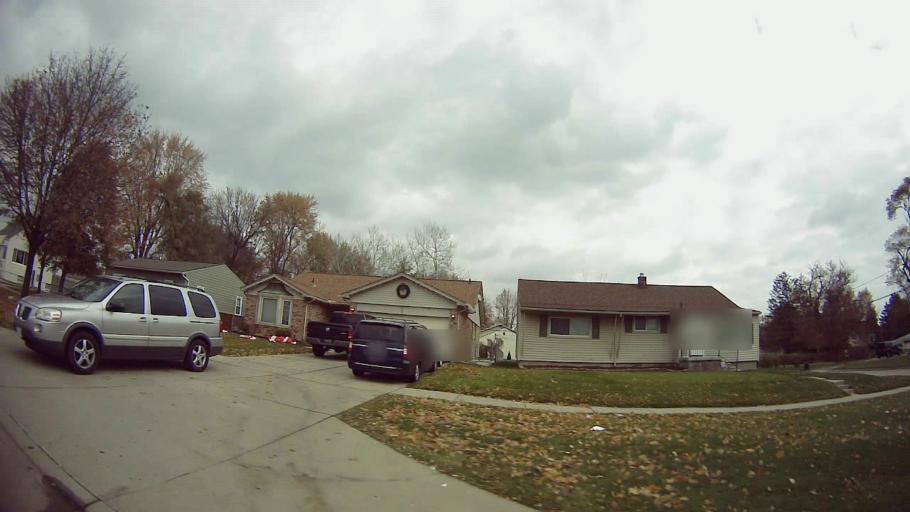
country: US
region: Michigan
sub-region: Oakland County
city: Madison Heights
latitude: 42.5316
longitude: -83.0683
